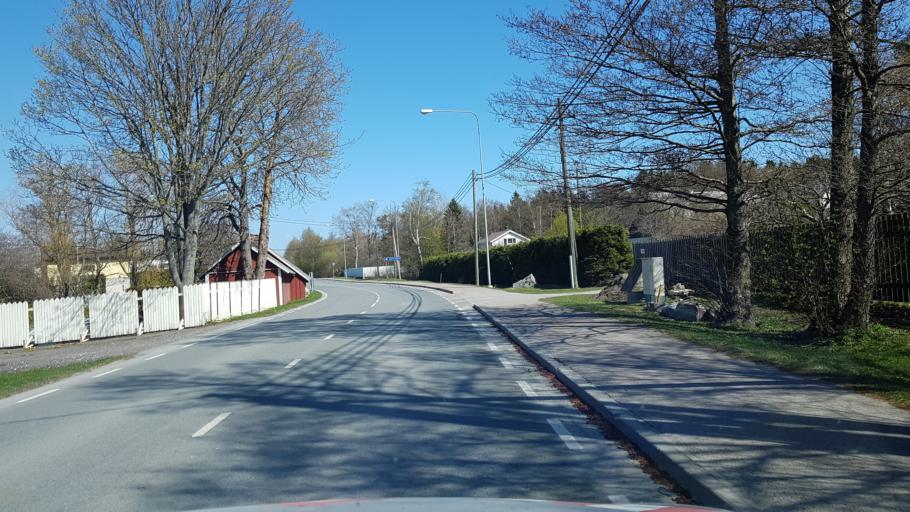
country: EE
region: Harju
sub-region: Viimsi vald
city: Rummu
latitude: 59.5575
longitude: 24.7968
